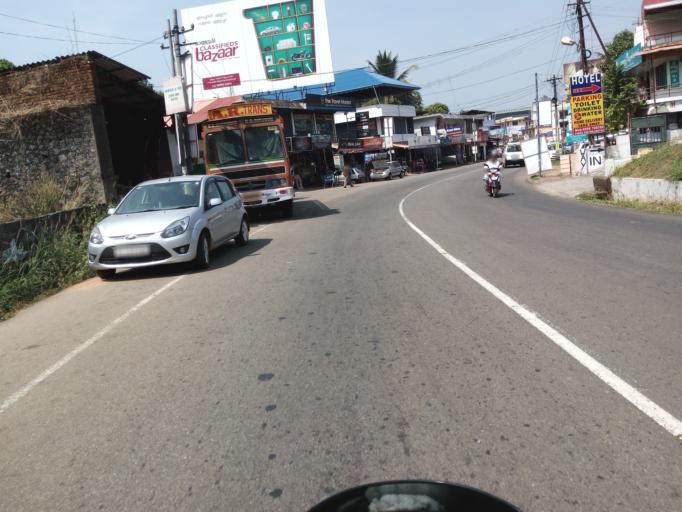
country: IN
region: Kerala
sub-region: Ernakulam
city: Muvattupula
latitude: 9.9048
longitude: 76.7106
